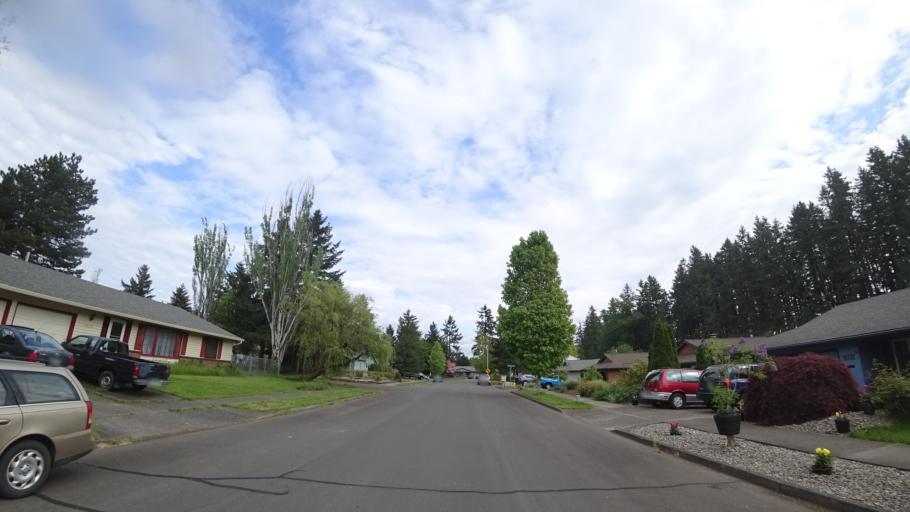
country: US
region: Oregon
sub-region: Washington County
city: Hillsboro
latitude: 45.4995
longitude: -122.9561
